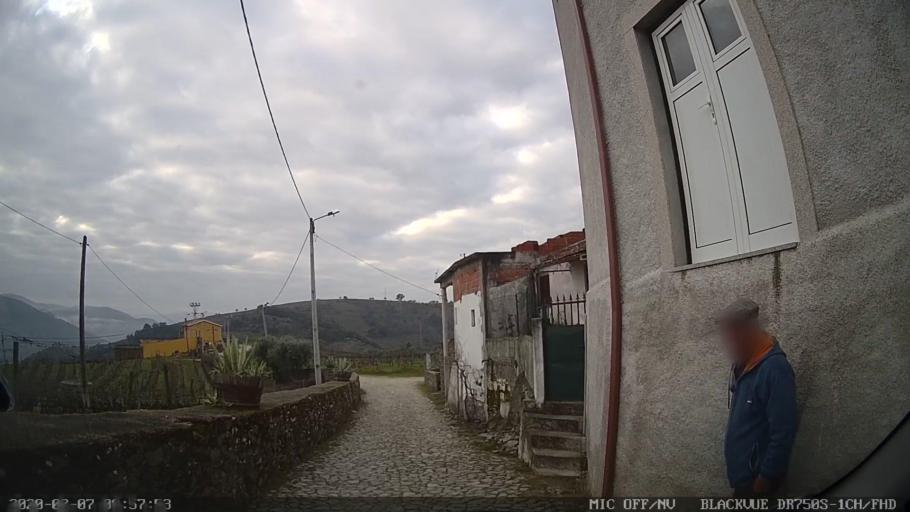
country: PT
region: Vila Real
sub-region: Sabrosa
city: Sabrosa
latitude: 41.2094
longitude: -7.5291
